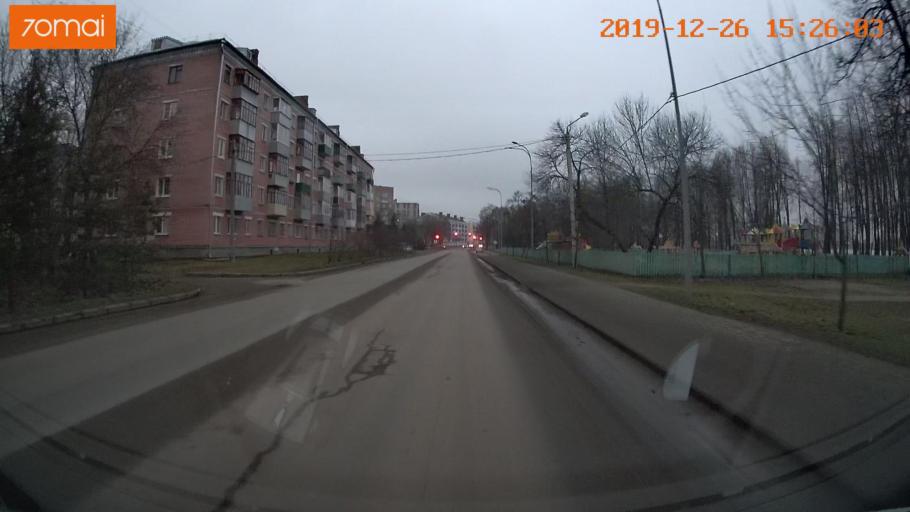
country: RU
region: Jaroslavl
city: Rybinsk
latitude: 58.0557
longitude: 38.8319
